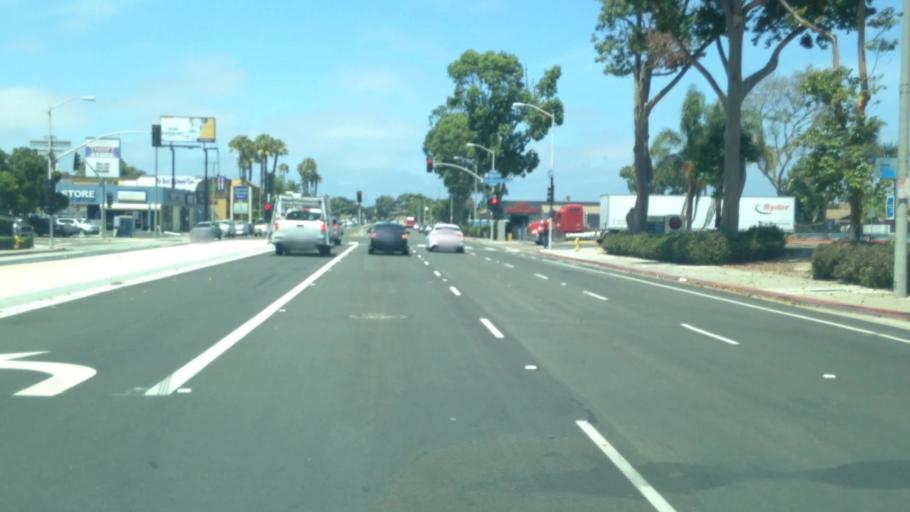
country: US
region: California
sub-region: San Diego County
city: San Diego
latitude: 32.7540
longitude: -117.2130
